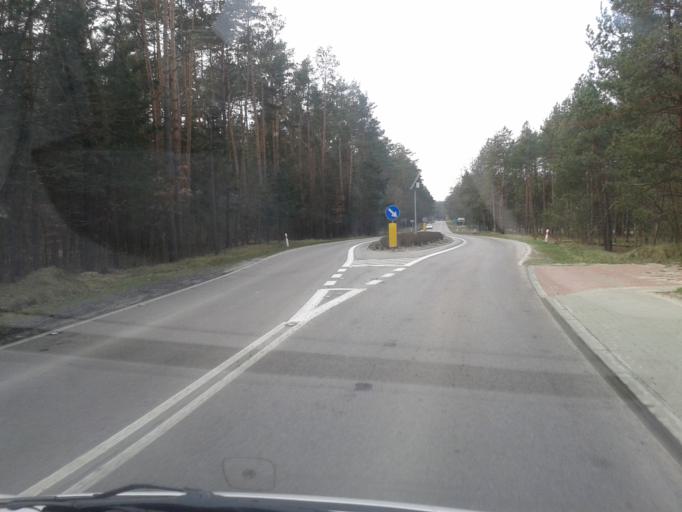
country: PL
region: Lublin Voivodeship
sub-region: Powiat tomaszowski
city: Belzec
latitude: 50.3776
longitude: 23.3926
